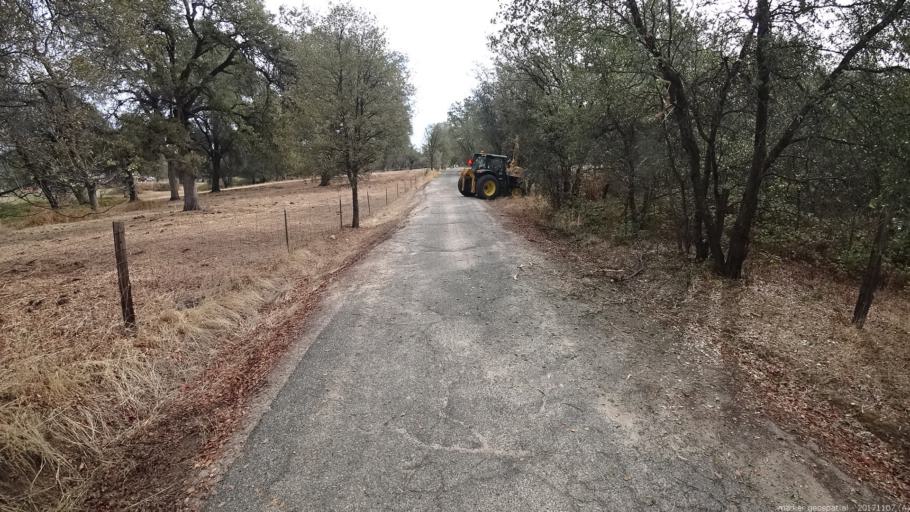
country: US
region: California
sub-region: Shasta County
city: Shasta
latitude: 40.5045
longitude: -122.5801
